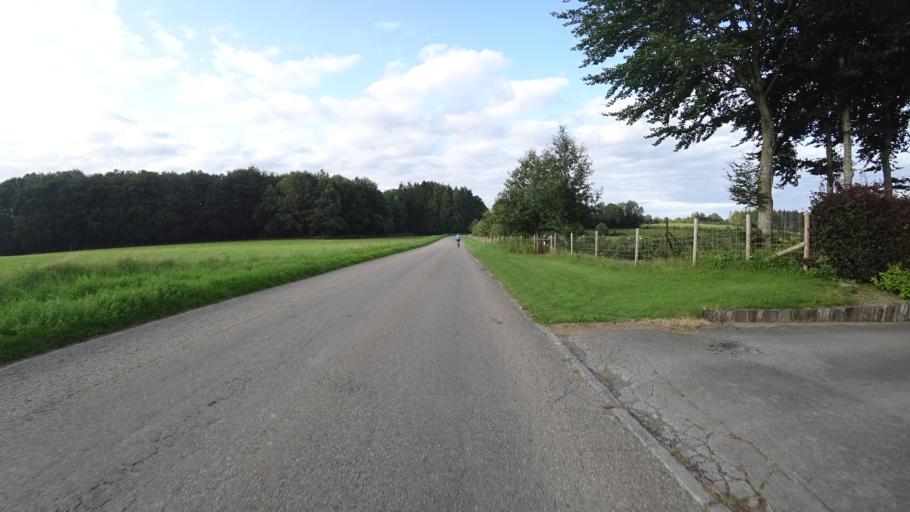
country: BE
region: Wallonia
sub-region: Province du Luxembourg
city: Bertrix
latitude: 49.8358
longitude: 5.3415
